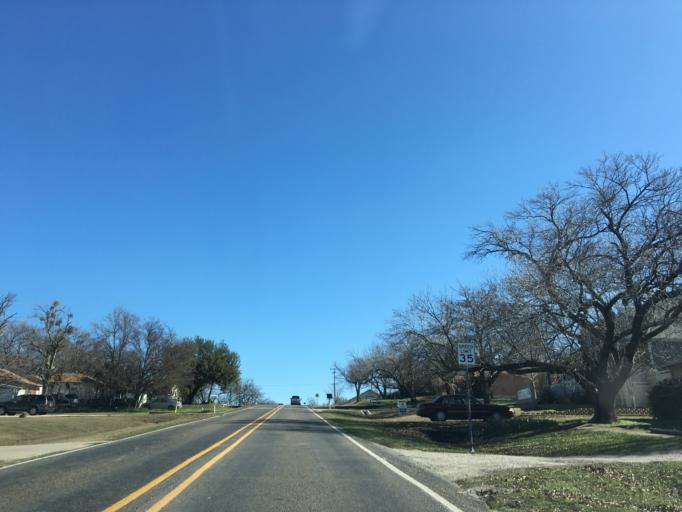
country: US
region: Texas
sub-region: Collin County
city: Prosper
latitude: 33.2358
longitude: -96.7994
